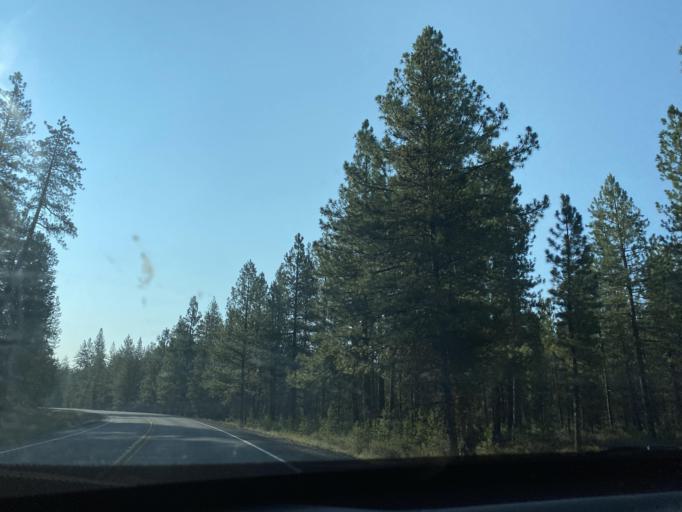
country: US
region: Oregon
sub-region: Deschutes County
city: La Pine
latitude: 43.7071
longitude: -121.4013
